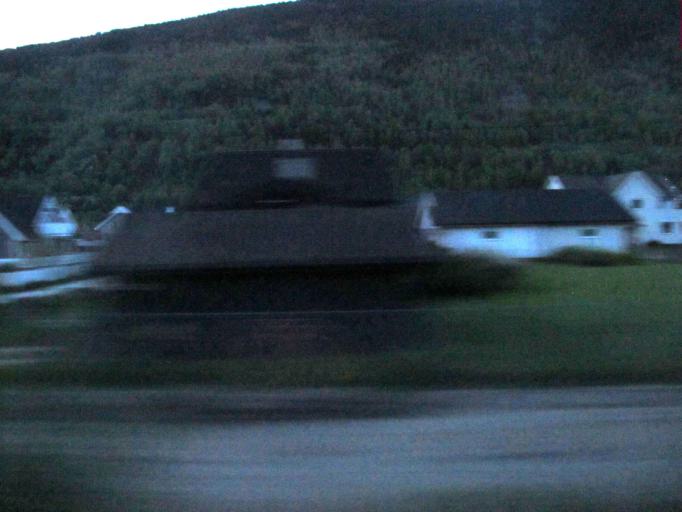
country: NO
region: Oppland
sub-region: Sel
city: Otta
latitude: 61.7658
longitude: 9.5385
